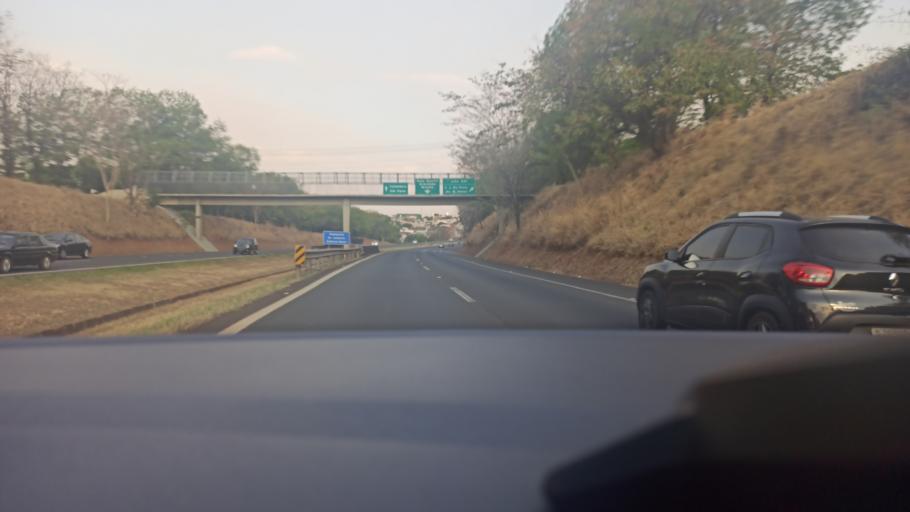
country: BR
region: Sao Paulo
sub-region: Sao Jose Do Rio Preto
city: Sao Jose do Rio Preto
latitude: -20.8241
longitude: -49.3709
